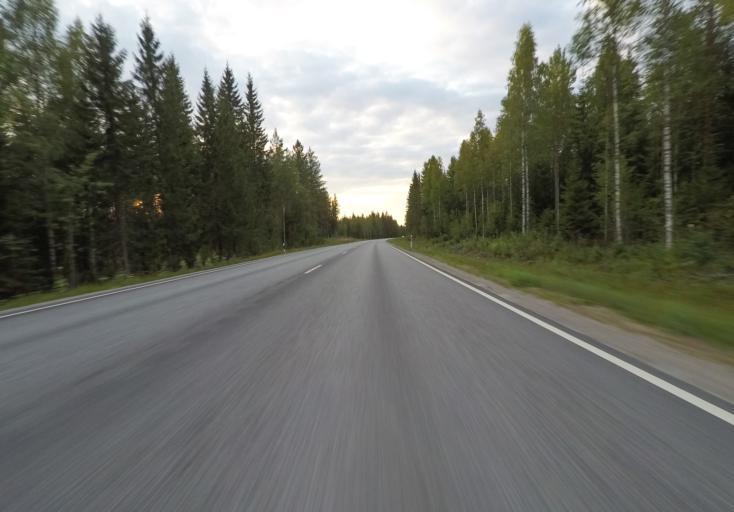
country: FI
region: Central Finland
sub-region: Jyvaeskylae
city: Toivakka
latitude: 62.2350
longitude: 26.1861
